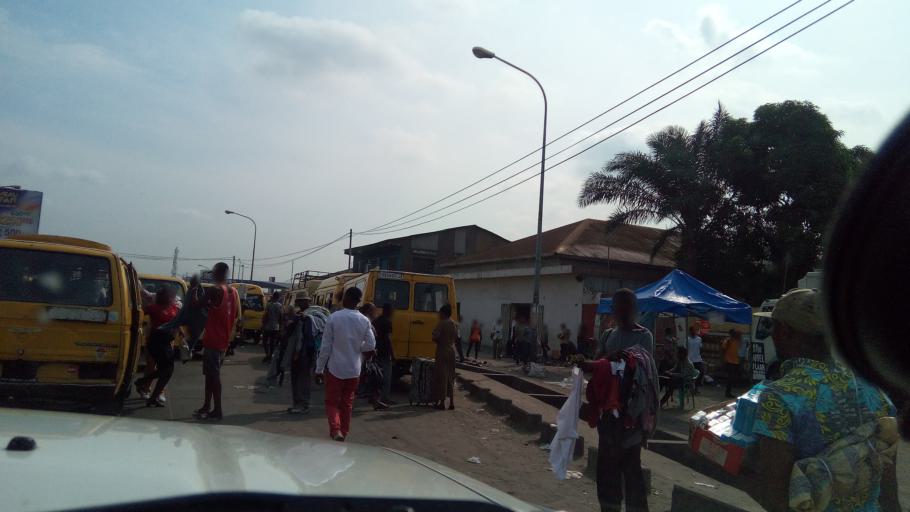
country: CD
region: Kinshasa
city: Kinshasa
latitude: -4.3481
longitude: 15.3114
